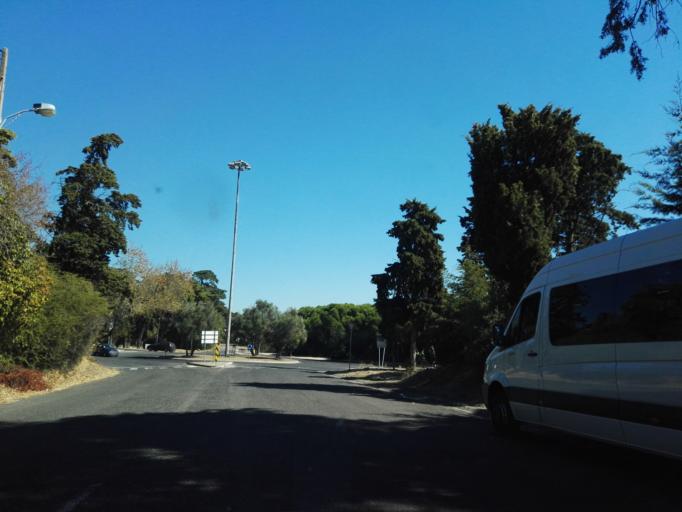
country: PT
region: Lisbon
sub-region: Oeiras
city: Alges
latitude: 38.7181
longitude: -9.2000
